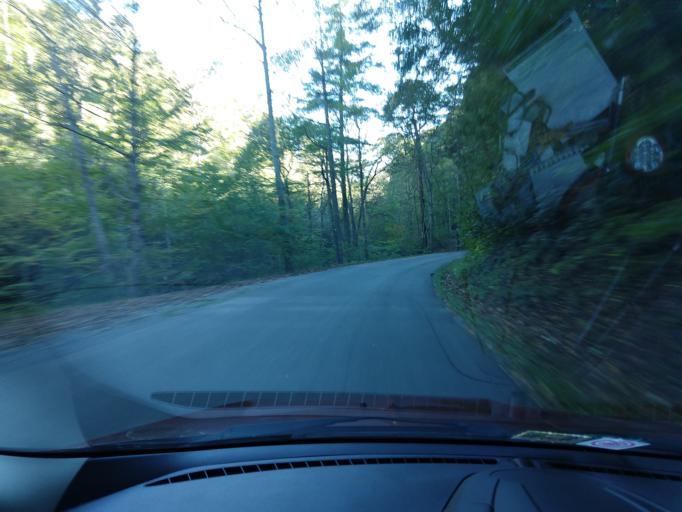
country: US
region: Virginia
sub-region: Alleghany County
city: Clifton Forge
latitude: 37.8552
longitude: -79.8600
